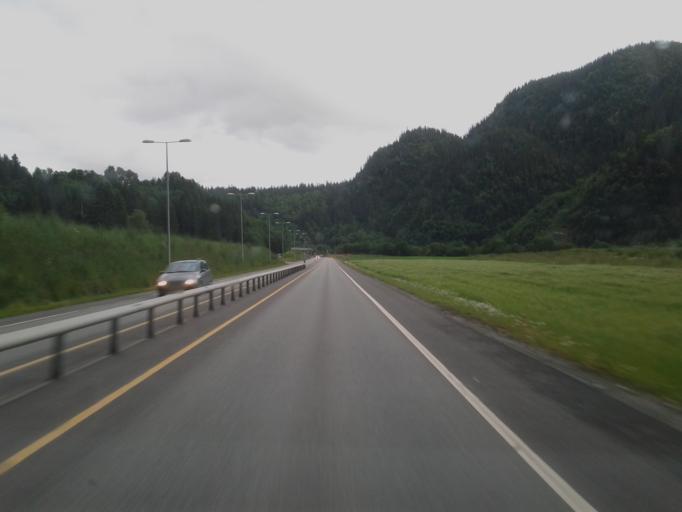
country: NO
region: Sor-Trondelag
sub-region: Midtre Gauldal
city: Storen
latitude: 63.0746
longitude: 10.2634
